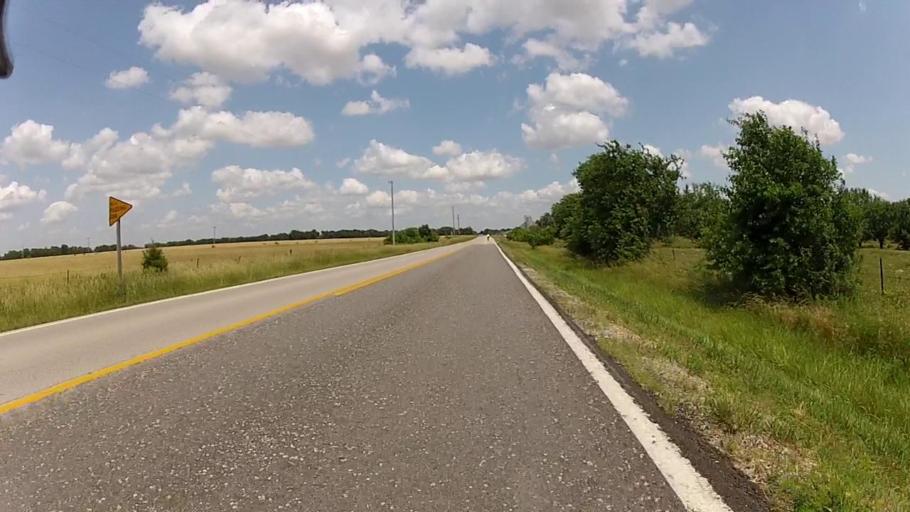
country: US
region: Kansas
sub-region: Labette County
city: Altamont
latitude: 37.1926
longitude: -95.3422
